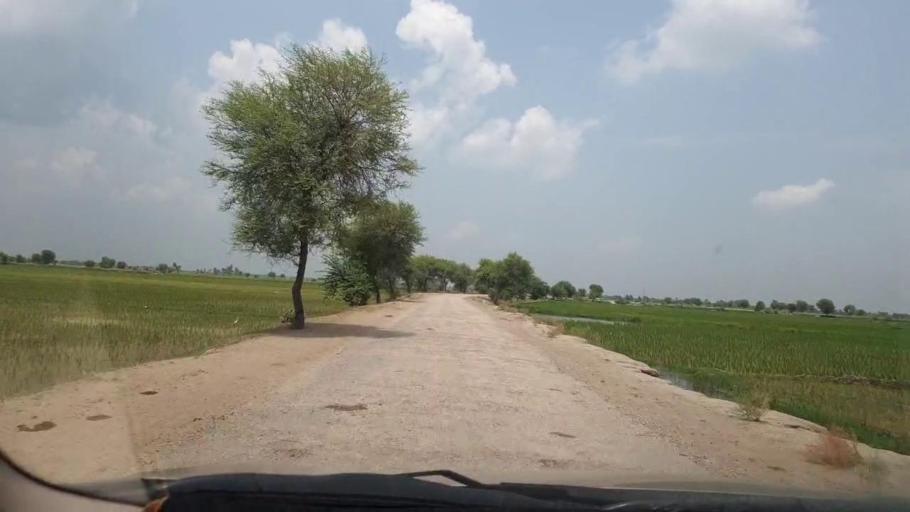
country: PK
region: Sindh
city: Larkana
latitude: 27.6057
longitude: 68.1438
